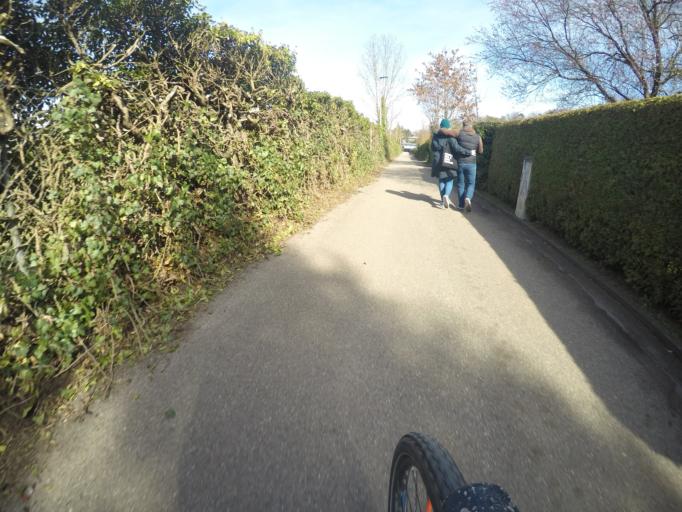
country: DE
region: Baden-Wuerttemberg
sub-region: Regierungsbezirk Stuttgart
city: Korntal
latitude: 48.8089
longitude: 9.1241
